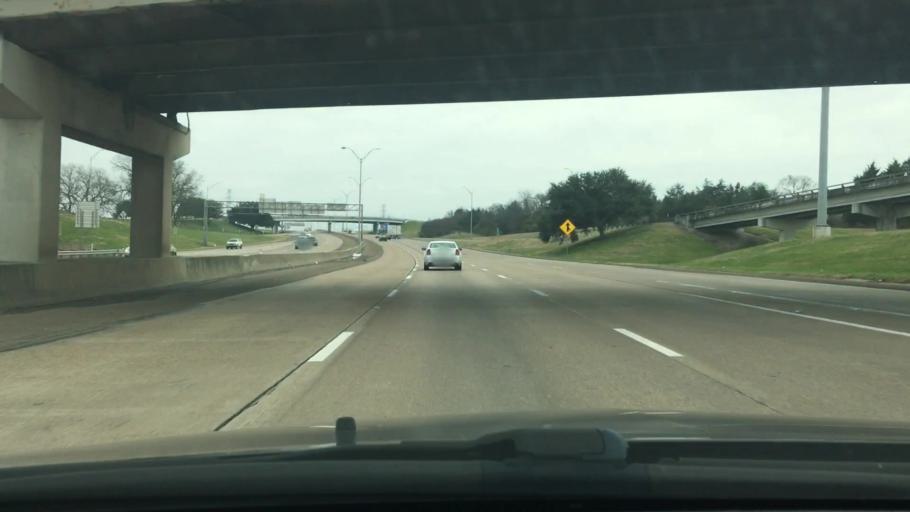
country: US
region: Texas
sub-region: Dallas County
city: Hutchins
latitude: 32.6602
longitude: -96.7249
